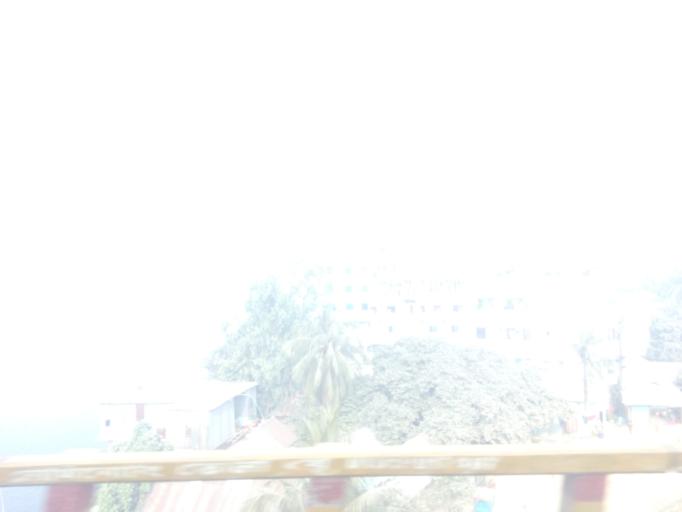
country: BD
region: Dhaka
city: Narayanganj
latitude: 23.7043
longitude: 90.5186
